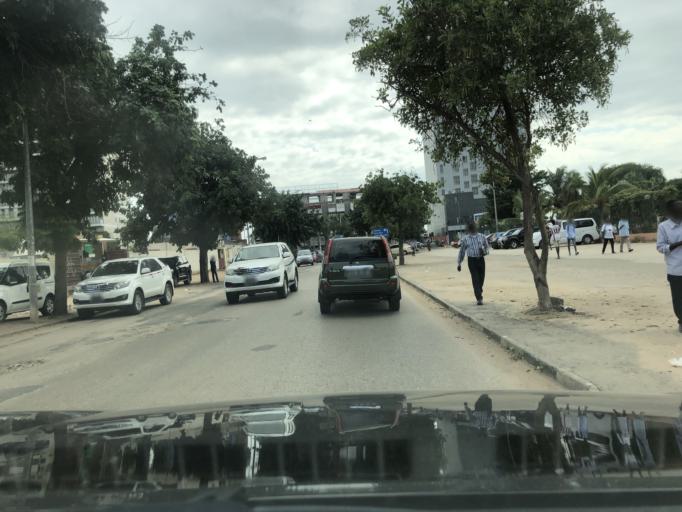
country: AO
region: Luanda
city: Luanda
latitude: -8.8317
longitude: 13.2387
